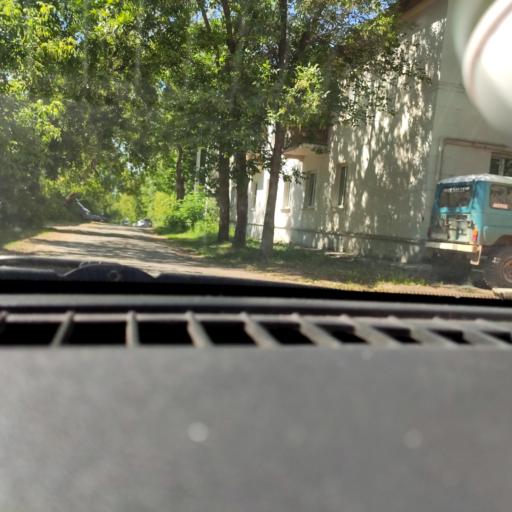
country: RU
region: Perm
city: Polazna
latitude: 58.1253
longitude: 56.3808
